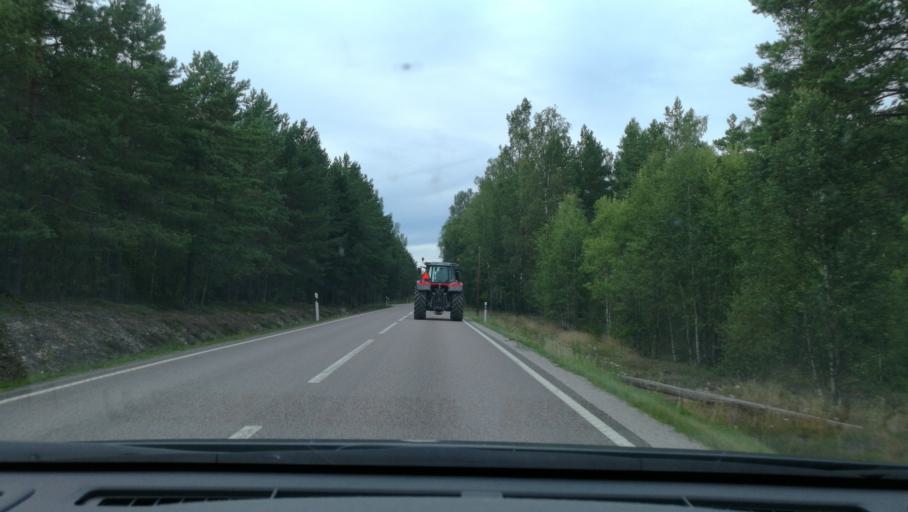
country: SE
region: Vaestmanland
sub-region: Kungsors Kommun
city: Kungsoer
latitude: 59.3307
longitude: 16.1121
